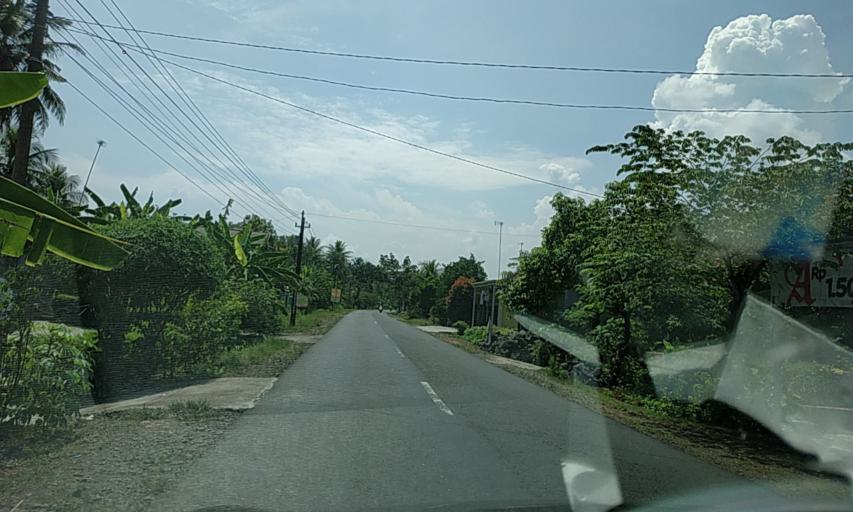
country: ID
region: Central Java
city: Mulyosari
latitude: -7.5147
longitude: 108.7839
